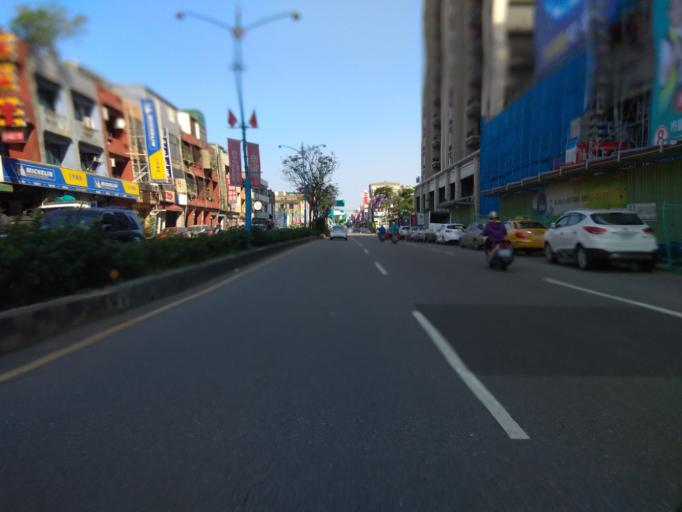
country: TW
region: Taiwan
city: Daxi
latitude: 24.9157
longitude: 121.1804
